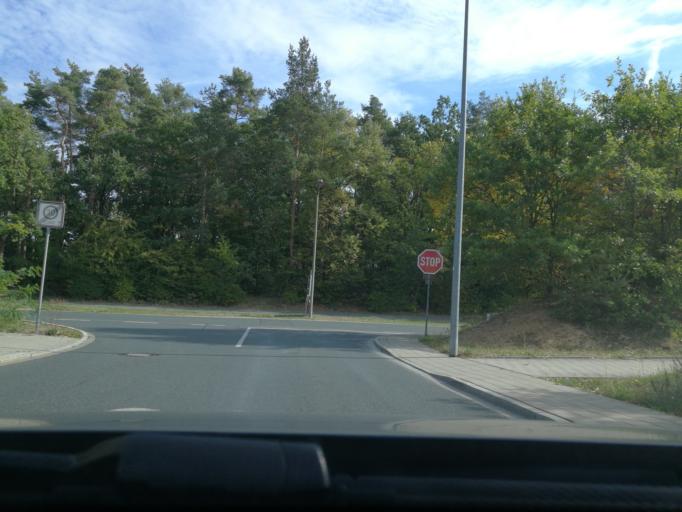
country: DE
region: Bavaria
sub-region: Regierungsbezirk Mittelfranken
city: Furth
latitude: 49.5050
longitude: 10.9661
